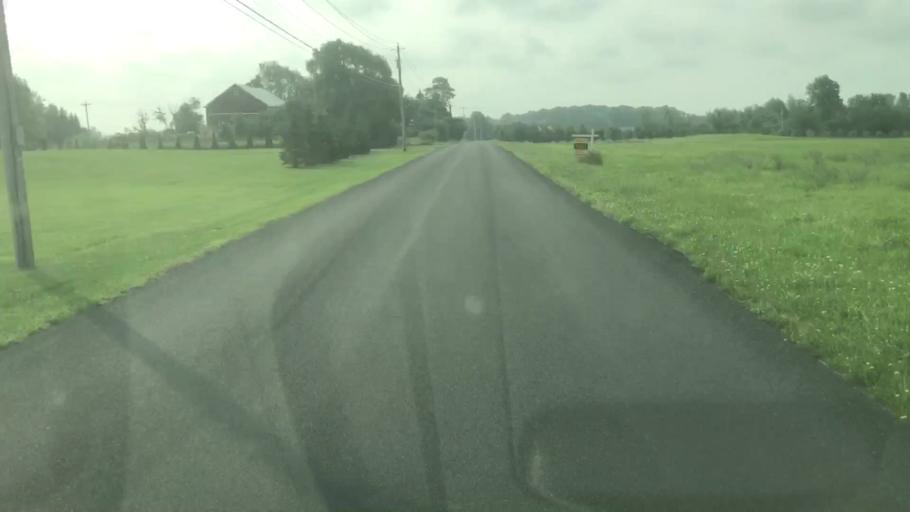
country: US
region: New York
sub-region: Onondaga County
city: Skaneateles
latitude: 42.9089
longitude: -76.4528
